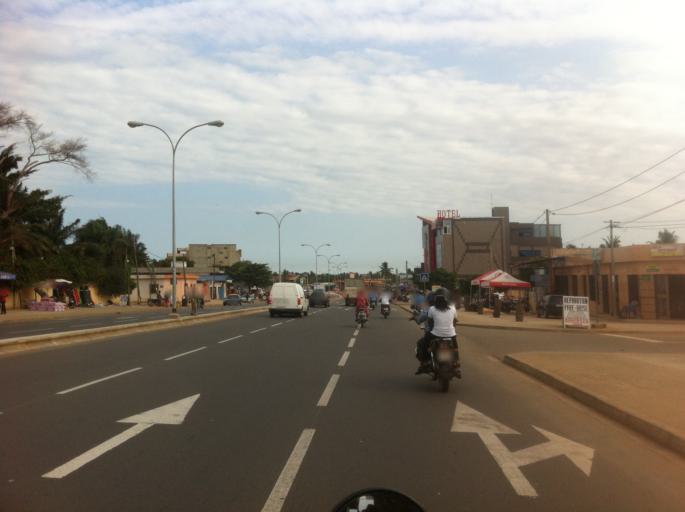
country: TG
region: Maritime
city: Lome
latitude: 6.1519
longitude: 1.2013
